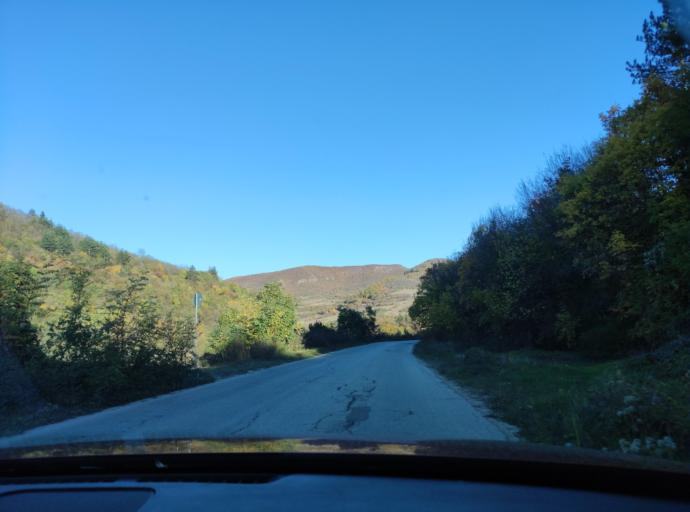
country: BG
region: Montana
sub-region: Obshtina Chiprovtsi
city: Chiprovtsi
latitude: 43.3808
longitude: 22.9046
